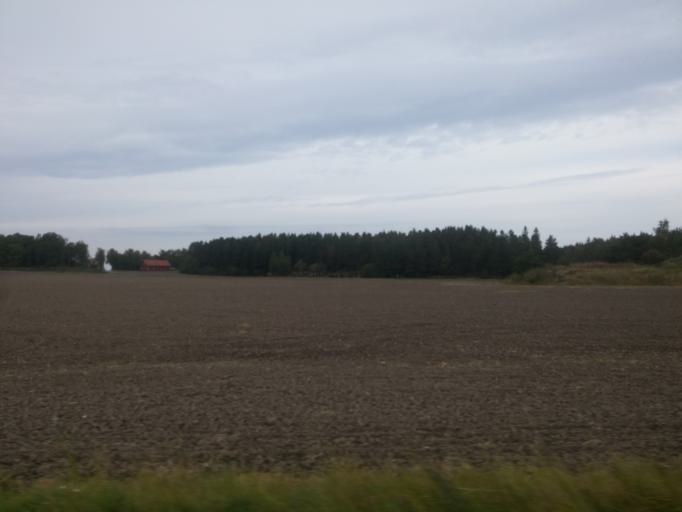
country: SE
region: OEstergoetland
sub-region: Norrkopings Kommun
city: Krokek
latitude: 58.5758
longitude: 16.4784
